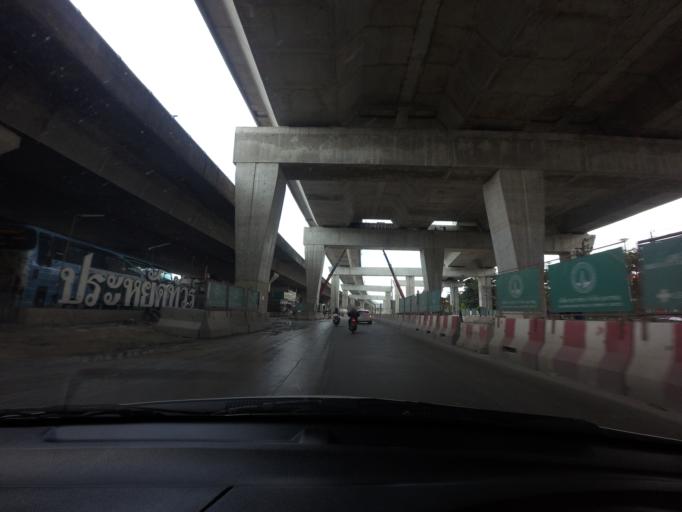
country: TH
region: Bangkok
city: Bang Sue
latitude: 13.8149
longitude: 100.5502
